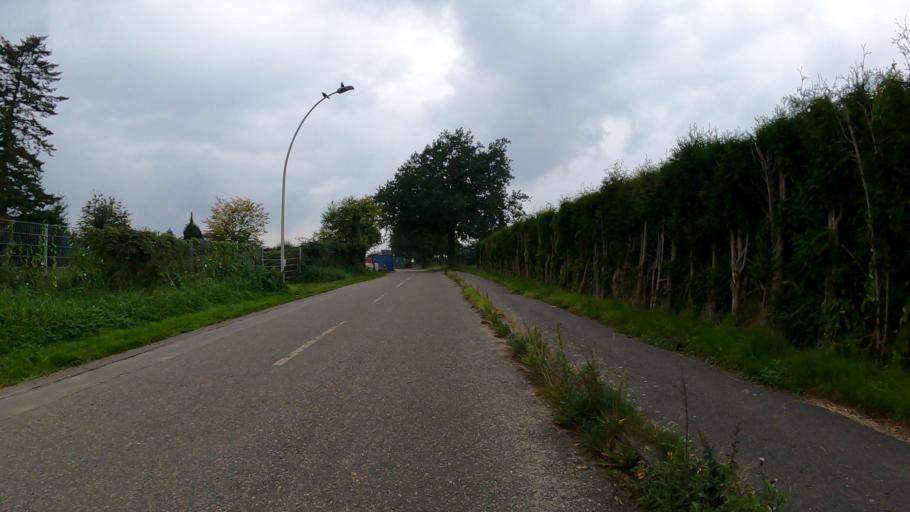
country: DE
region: Schleswig-Holstein
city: Halstenbek
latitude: 53.6301
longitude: 9.8296
